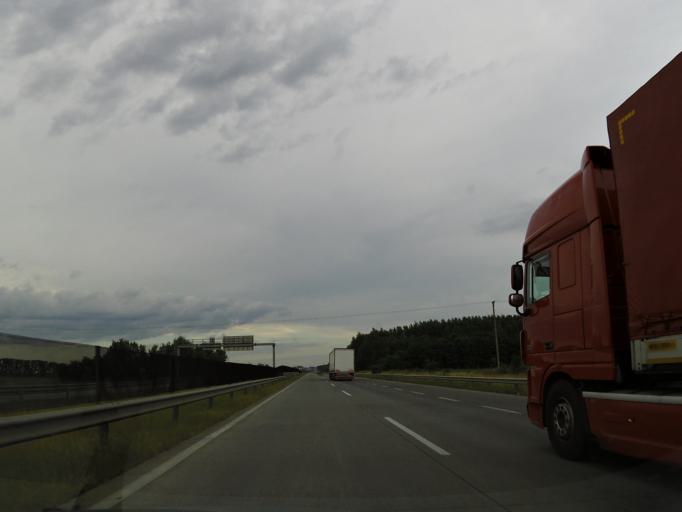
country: HU
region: Pest
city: Gyal
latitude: 47.3680
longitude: 19.2368
